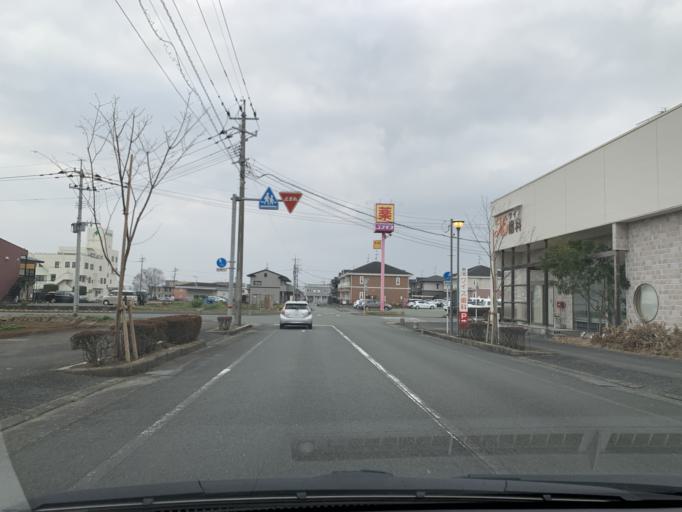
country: JP
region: Kumamoto
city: Ozu
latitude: 32.8765
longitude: 130.8638
